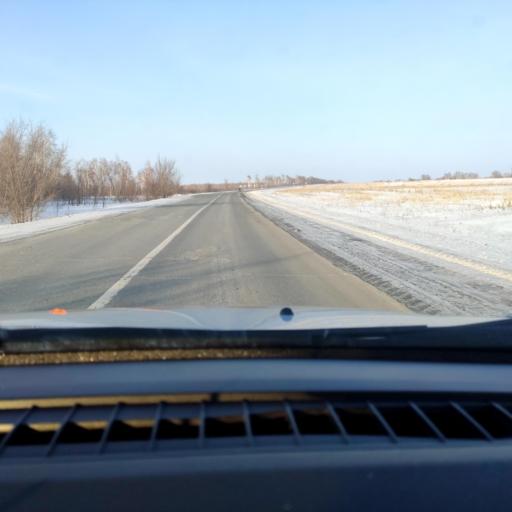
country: RU
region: Samara
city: Smyshlyayevka
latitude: 53.1057
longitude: 50.3502
